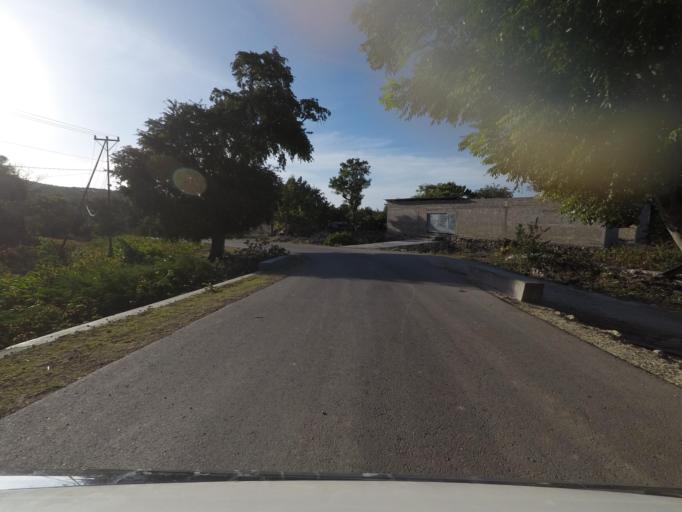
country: TL
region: Lautem
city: Lospalos
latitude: -8.3584
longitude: 127.0567
